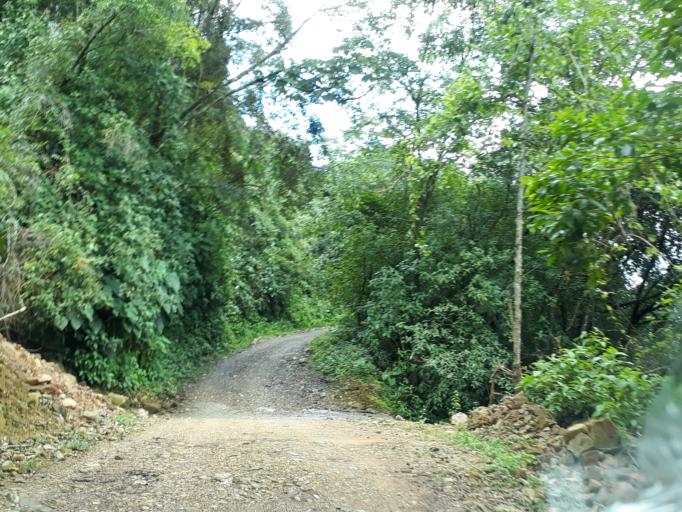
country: CO
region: Boyaca
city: Chivor
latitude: 4.7232
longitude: -73.3584
